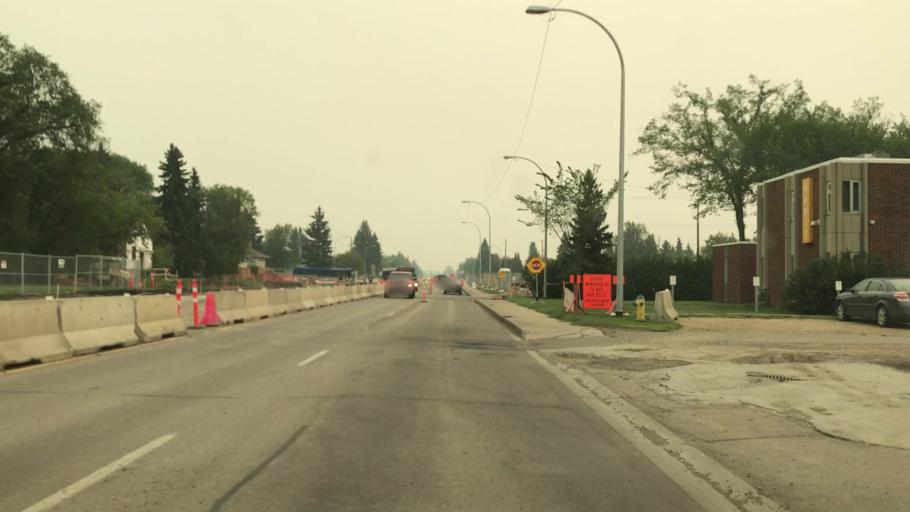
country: CA
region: Alberta
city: Edmonton
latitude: 53.5139
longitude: -113.4552
